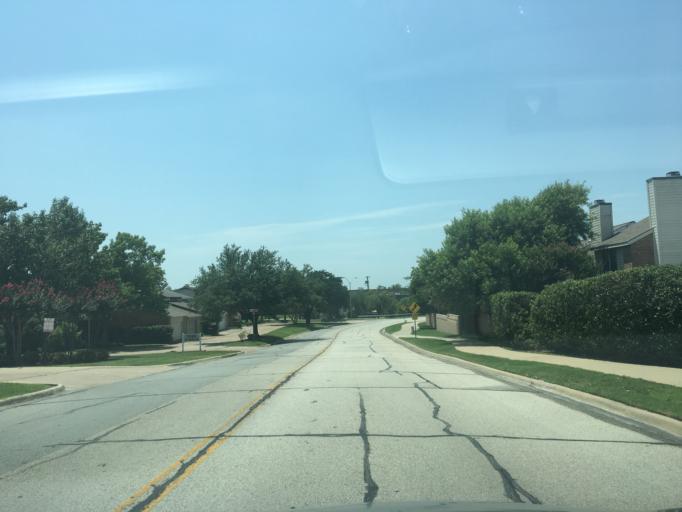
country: US
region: Texas
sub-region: Dallas County
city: Addison
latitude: 32.9496
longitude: -96.8572
